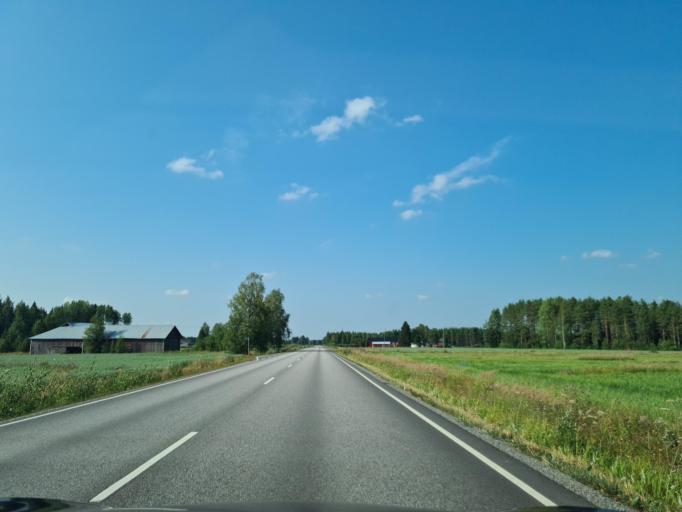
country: FI
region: Satakunta
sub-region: Pohjois-Satakunta
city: Karvia
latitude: 62.0437
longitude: 22.5143
